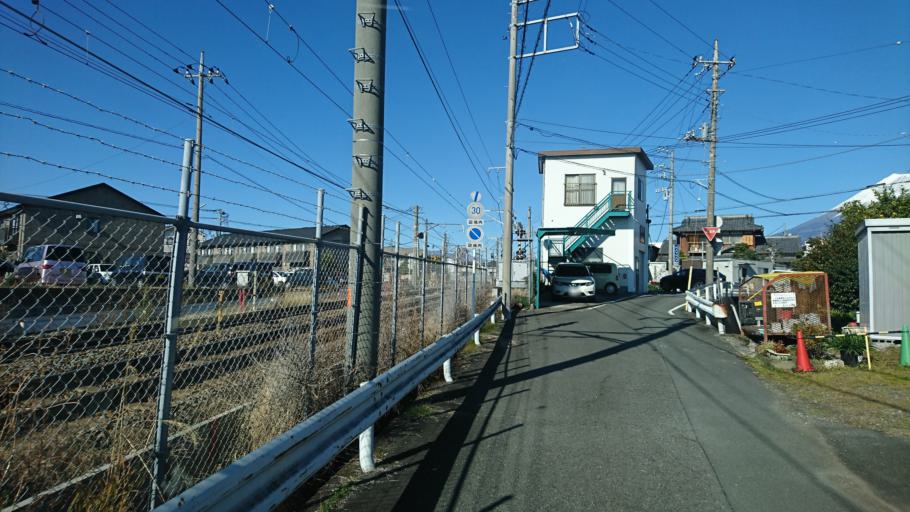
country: JP
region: Shizuoka
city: Fuji
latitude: 35.1792
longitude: 138.6550
